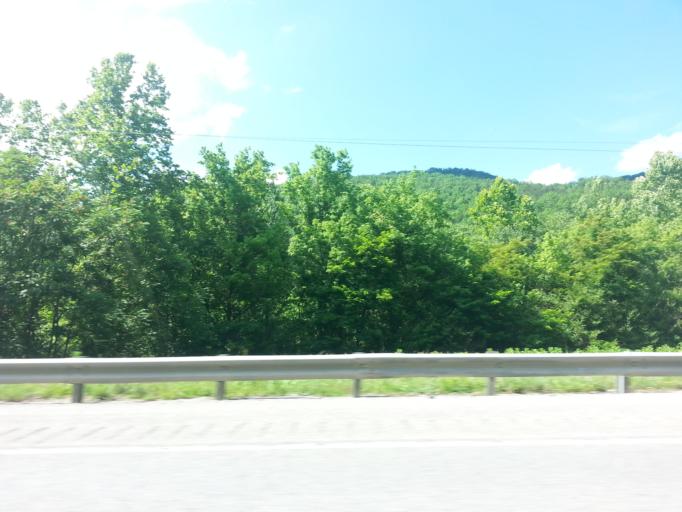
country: US
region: Kentucky
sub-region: Harlan County
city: Cumberland
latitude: 36.9448
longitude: -83.1122
